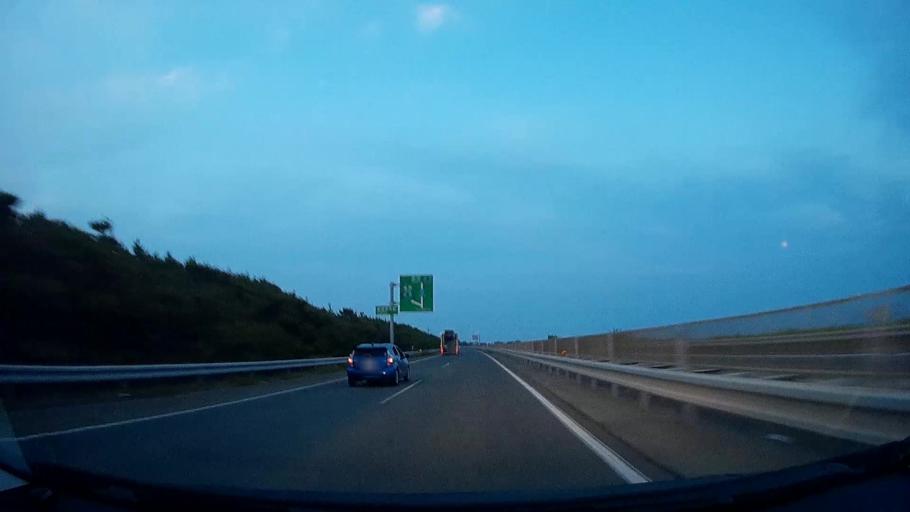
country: JP
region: Shizuoka
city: Kosai-shi
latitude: 34.6806
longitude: 137.5726
